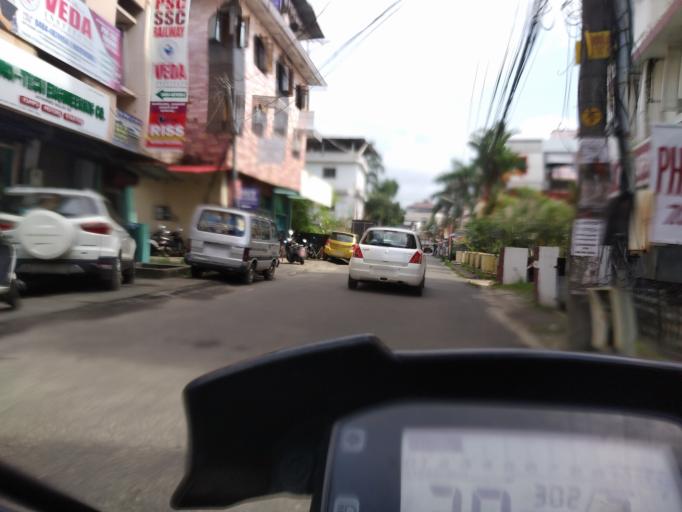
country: IN
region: Kerala
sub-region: Ernakulam
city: Cochin
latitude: 9.9871
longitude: 76.2854
